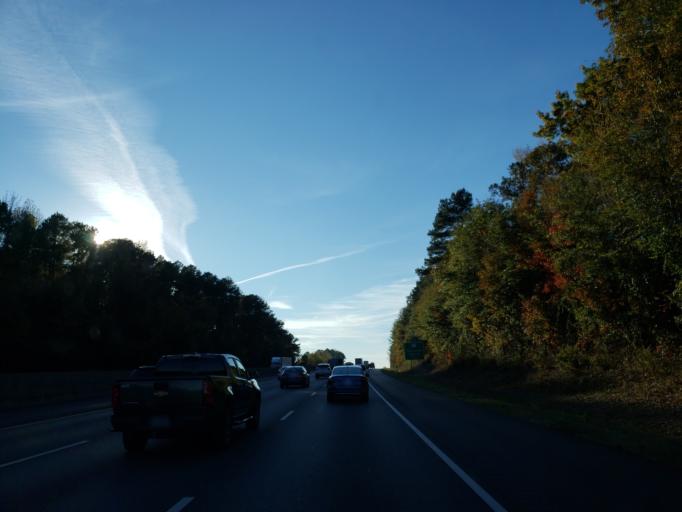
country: US
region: Alabama
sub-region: Tuscaloosa County
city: Coaling
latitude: 33.1777
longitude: -87.3806
